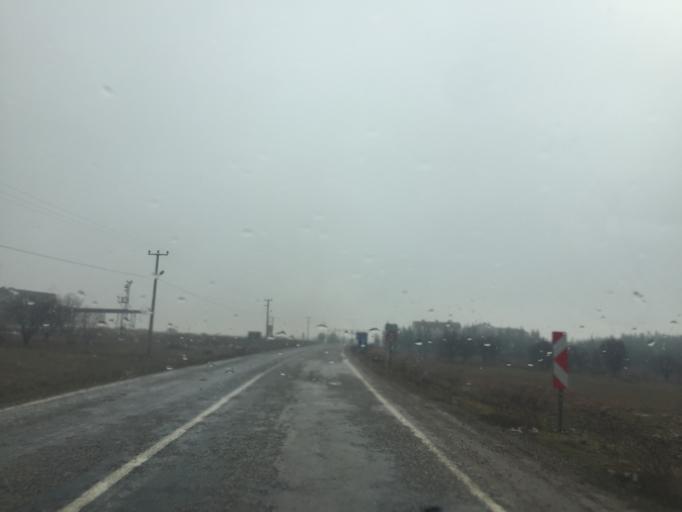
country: TR
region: Mardin
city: Omerli
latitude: 37.3973
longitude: 40.9303
